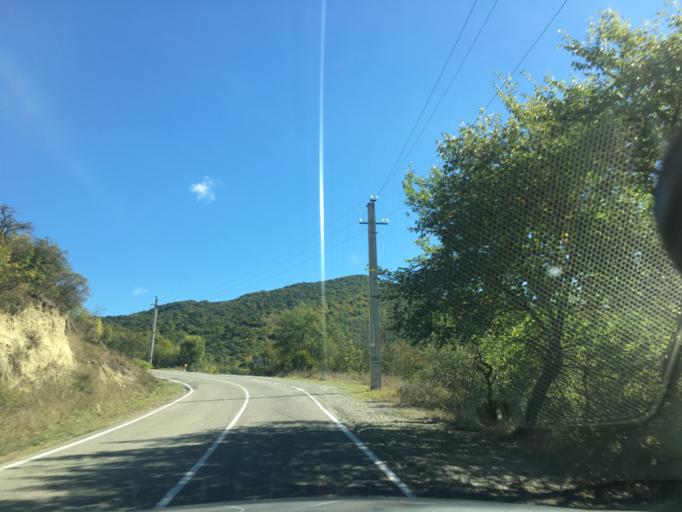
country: GE
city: Zahesi
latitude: 41.8430
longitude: 44.8845
